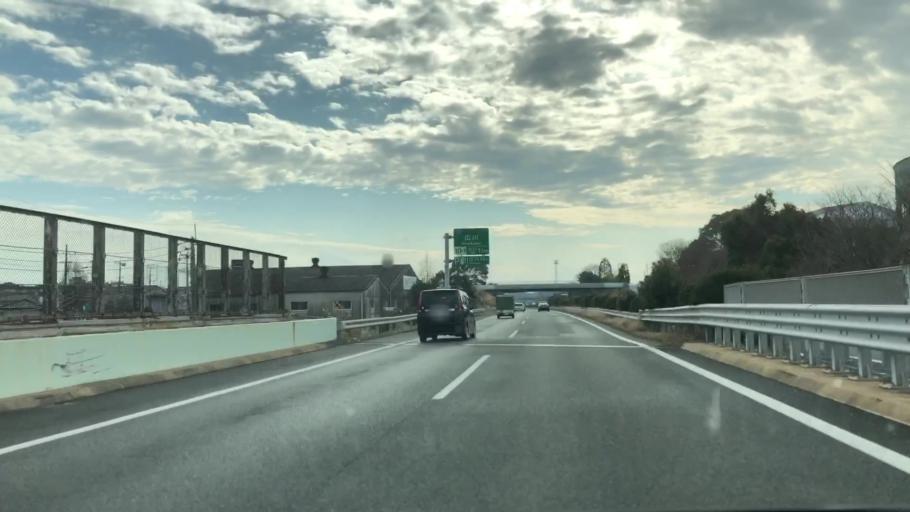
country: JP
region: Fukuoka
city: Kurume
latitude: 33.2665
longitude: 130.5391
